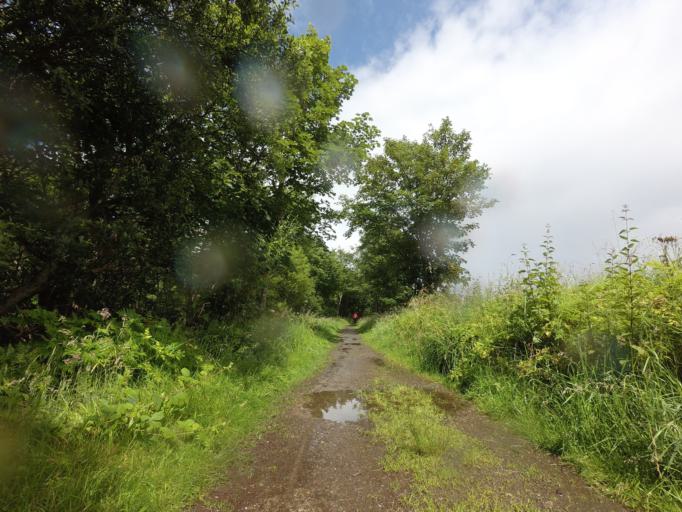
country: GB
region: Scotland
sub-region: Moray
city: Fochabers
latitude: 57.6668
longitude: -3.0915
